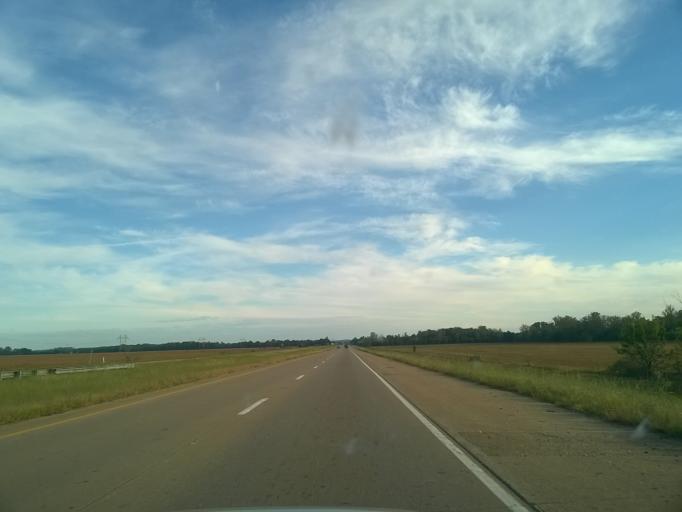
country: US
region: Indiana
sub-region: Vanderburgh County
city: Melody Hill
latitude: 38.0644
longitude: -87.4754
